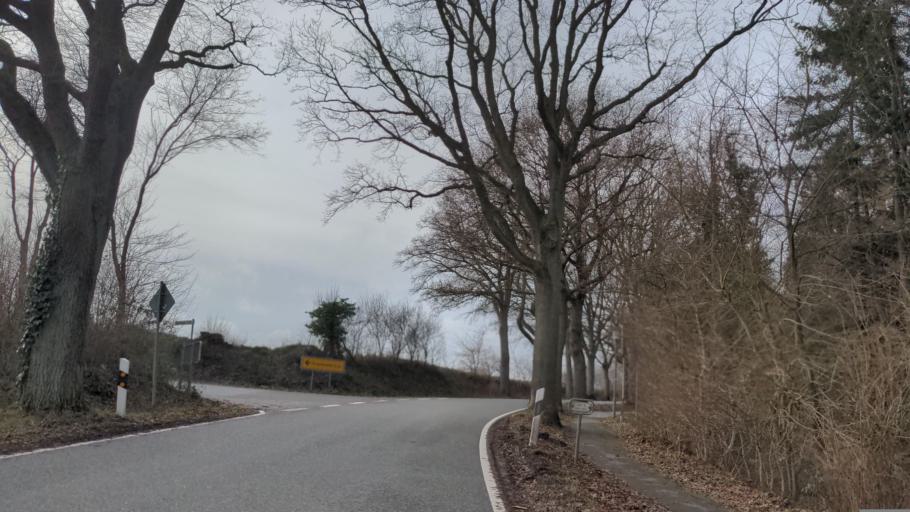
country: DE
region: Schleswig-Holstein
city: Neukirchen
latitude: 54.2042
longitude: 10.5844
